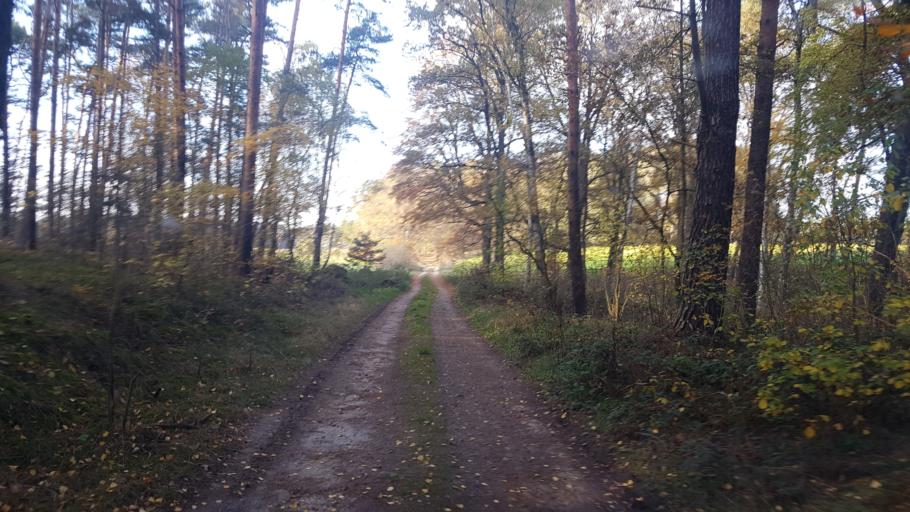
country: DE
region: Brandenburg
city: Calau
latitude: 51.6963
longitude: 13.9594
